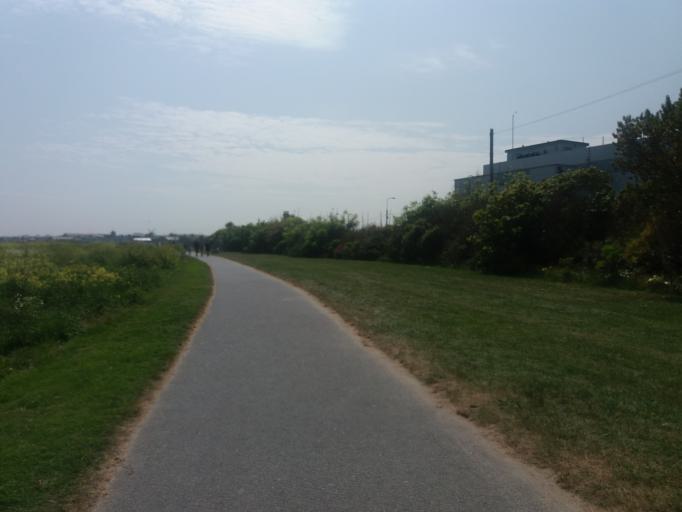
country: IE
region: Leinster
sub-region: Fingal County
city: Skerries
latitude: 53.5838
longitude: -6.1040
